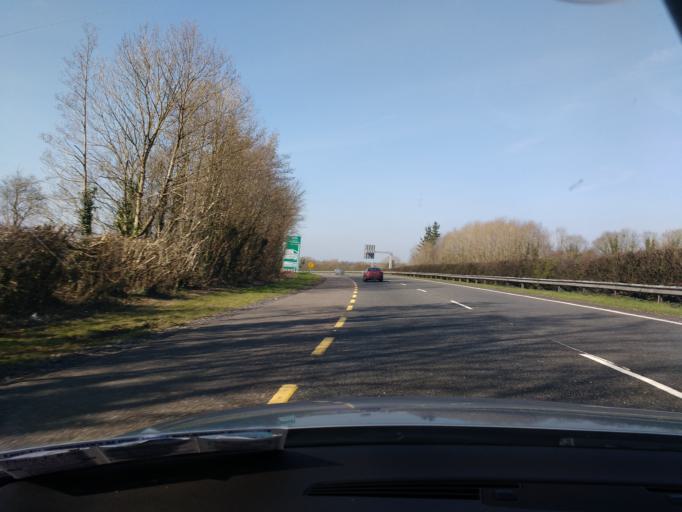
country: IE
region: Munster
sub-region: An Clar
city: Shannon
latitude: 52.7143
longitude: -8.8392
